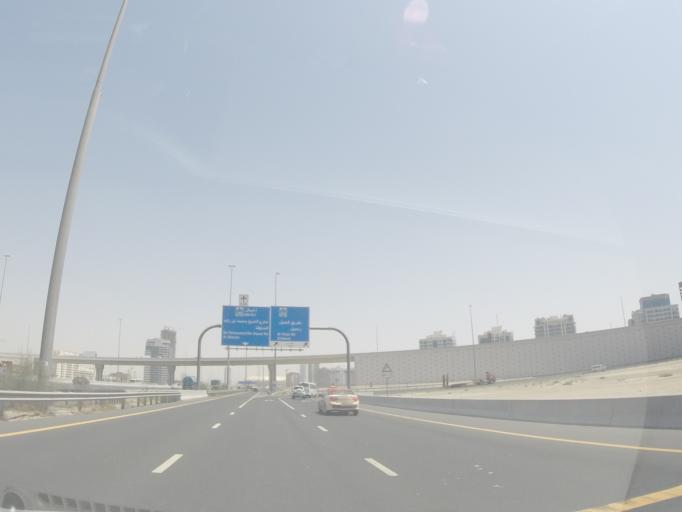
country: AE
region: Dubai
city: Dubai
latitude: 25.0425
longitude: 55.2020
